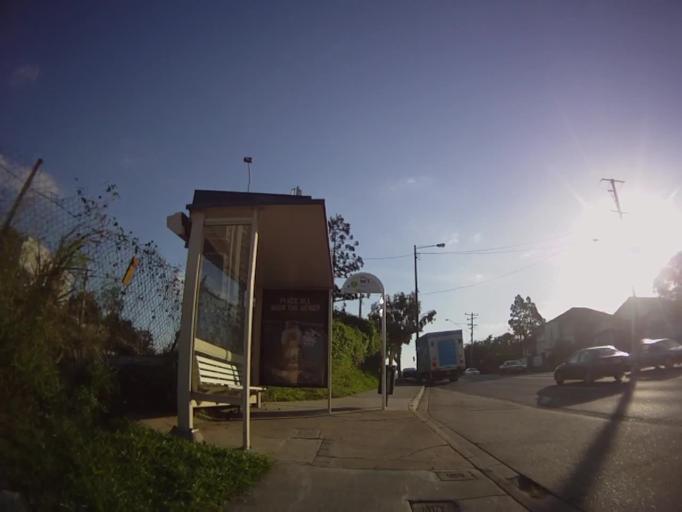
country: AU
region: Queensland
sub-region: Brisbane
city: Milton
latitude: -27.4695
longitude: 153.0032
